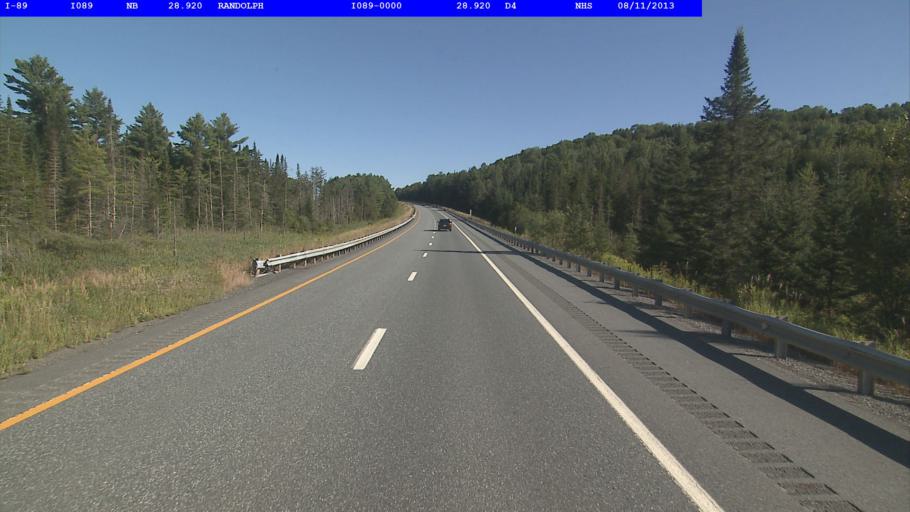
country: US
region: Vermont
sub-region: Orange County
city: Randolph
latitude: 43.9169
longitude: -72.6127
